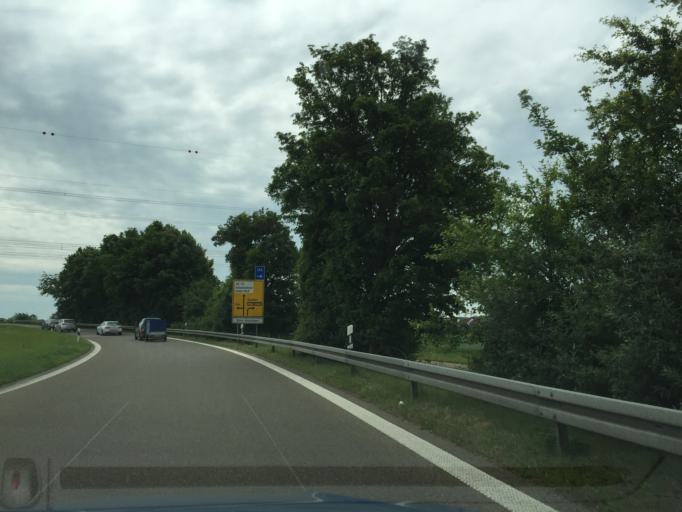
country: DE
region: Bavaria
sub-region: Swabia
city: Senden
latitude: 48.3371
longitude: 10.0322
